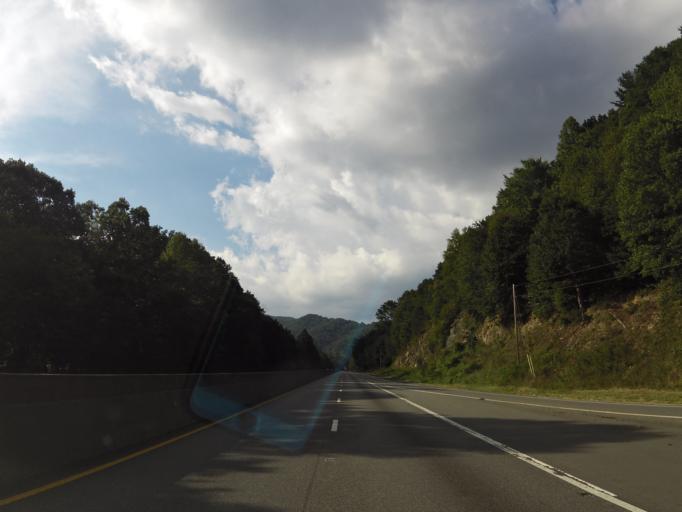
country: US
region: North Carolina
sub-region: Haywood County
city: Cove Creek
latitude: 35.6058
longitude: -83.0085
